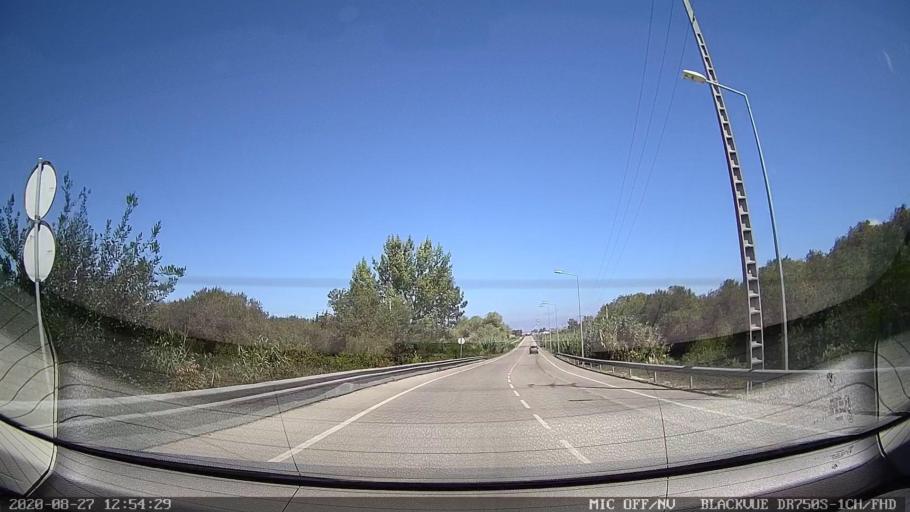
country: PT
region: Aveiro
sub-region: Ilhavo
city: Ilhavo
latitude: 40.5922
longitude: -8.6817
